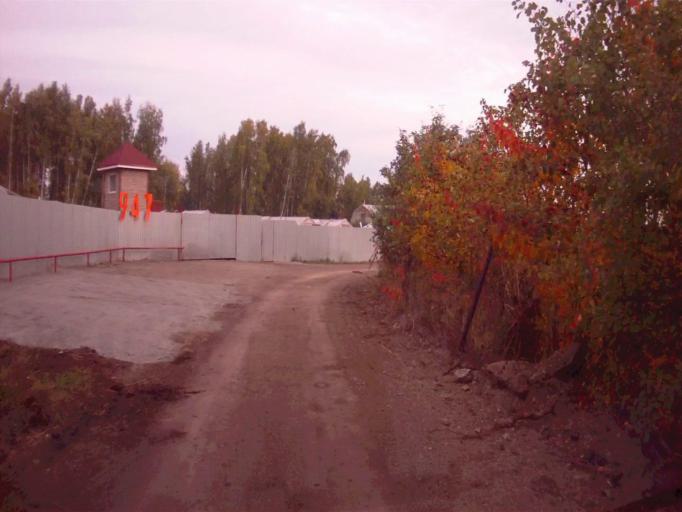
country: RU
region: Chelyabinsk
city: Sargazy
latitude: 55.1270
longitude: 61.2508
